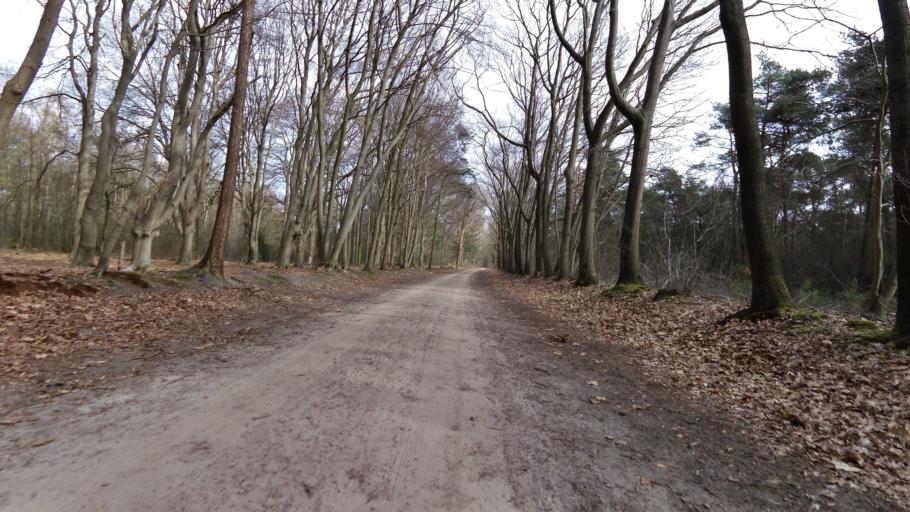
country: NL
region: Gelderland
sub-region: Gemeente Barneveld
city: Voorthuizen
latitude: 52.2169
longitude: 5.5815
